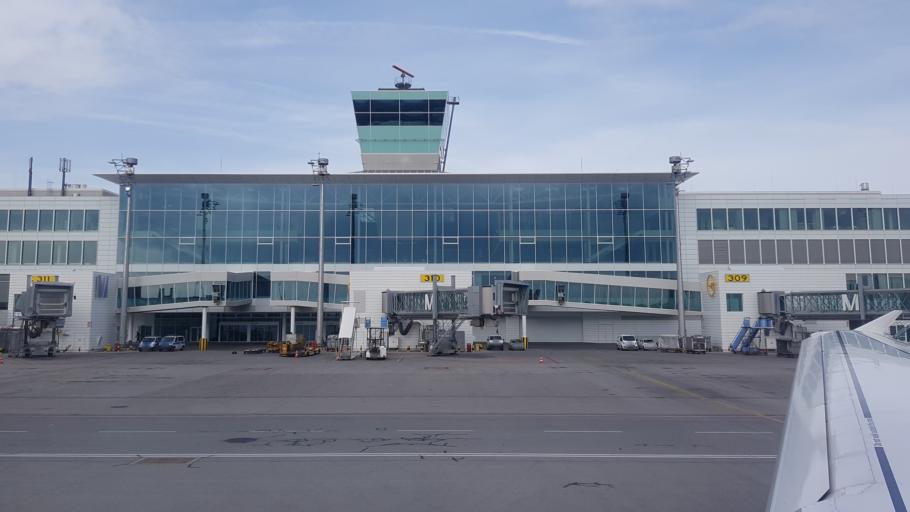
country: DE
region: Bavaria
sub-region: Upper Bavaria
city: Marzling
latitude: 48.3545
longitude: 11.7994
